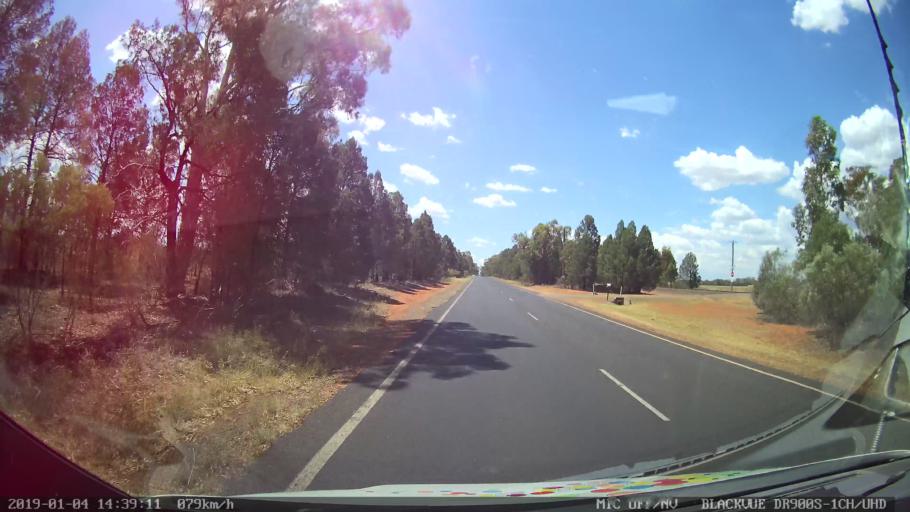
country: AU
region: New South Wales
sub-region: Dubbo Municipality
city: Dubbo
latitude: -32.1679
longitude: 148.6324
